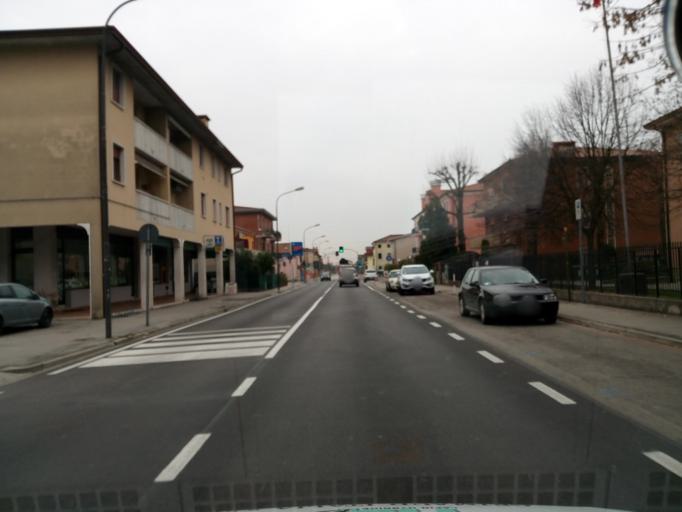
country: IT
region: Veneto
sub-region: Provincia di Padova
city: Pionca
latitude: 45.4670
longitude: 11.9621
